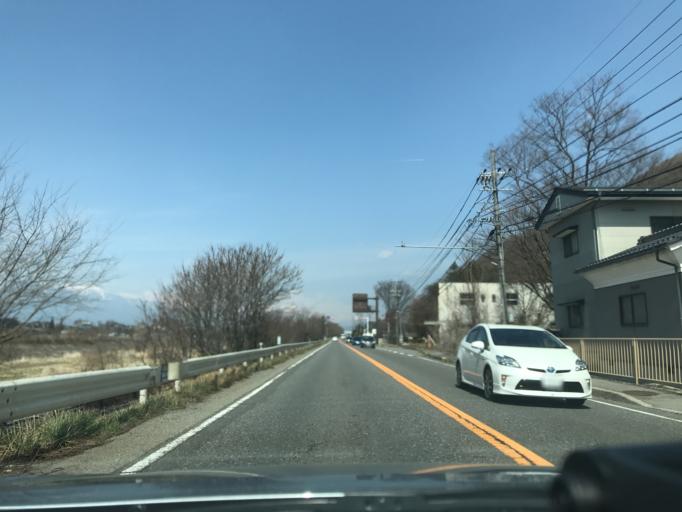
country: JP
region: Nagano
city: Matsumoto
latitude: 36.2555
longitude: 137.9502
